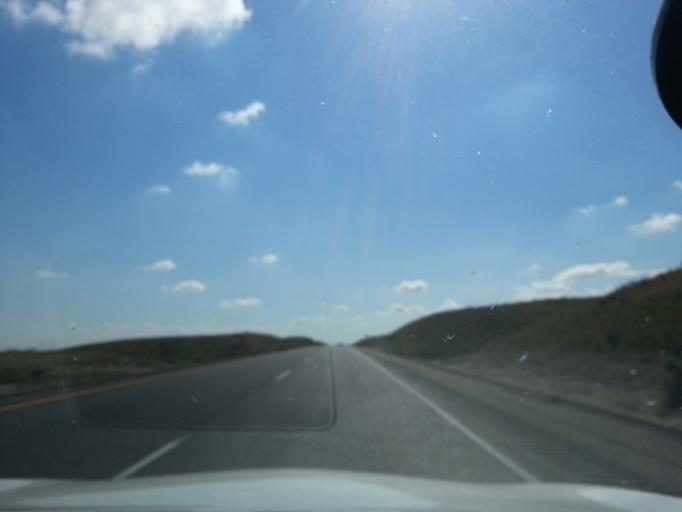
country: US
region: California
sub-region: Fresno County
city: Mendota
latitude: 36.4880
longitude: -120.4428
